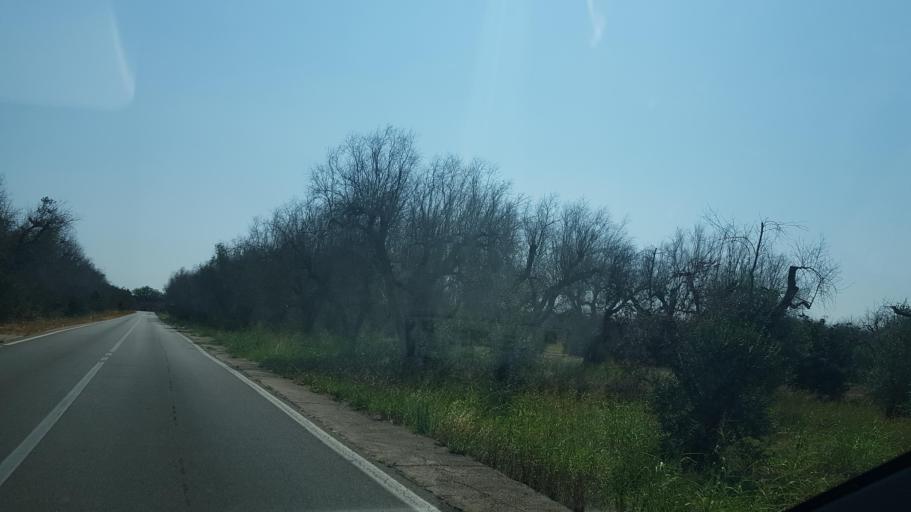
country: IT
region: Apulia
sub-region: Provincia di Lecce
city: Montesano Salentino
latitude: 40.0035
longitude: 18.3020
